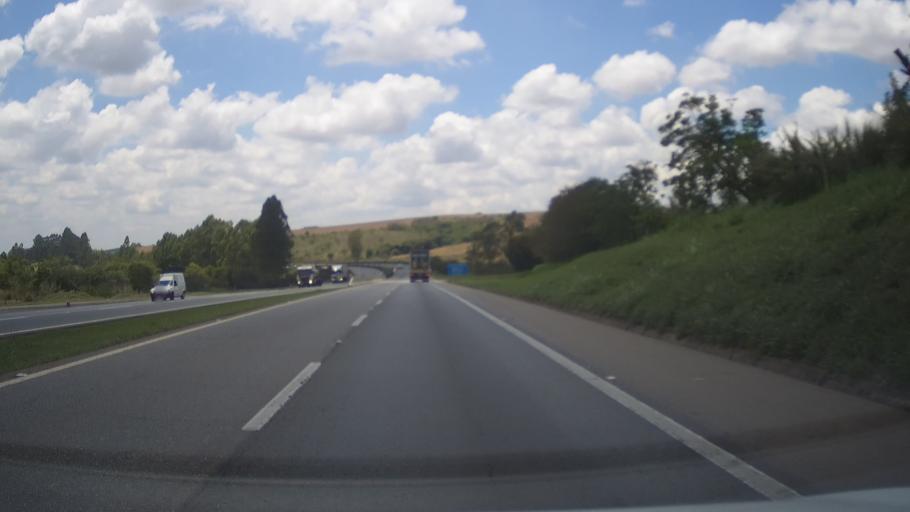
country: BR
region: Minas Gerais
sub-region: Campanha
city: Campanha
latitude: -21.7983
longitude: -45.4586
